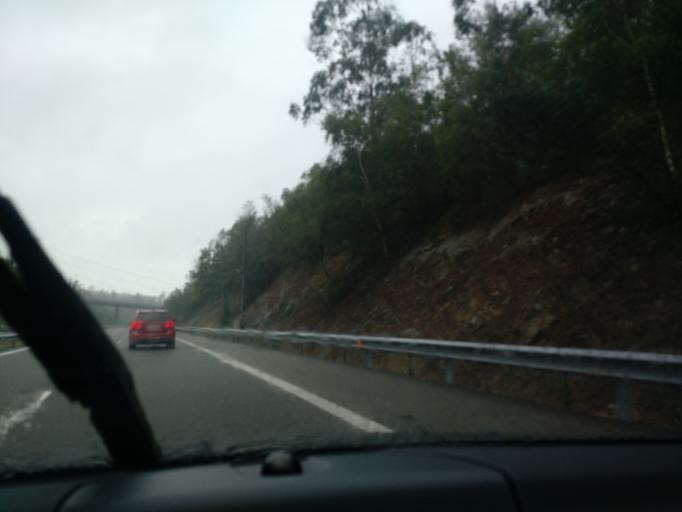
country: ES
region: Galicia
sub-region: Provincia da Coruna
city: Abegondo
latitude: 43.1569
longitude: -8.3263
